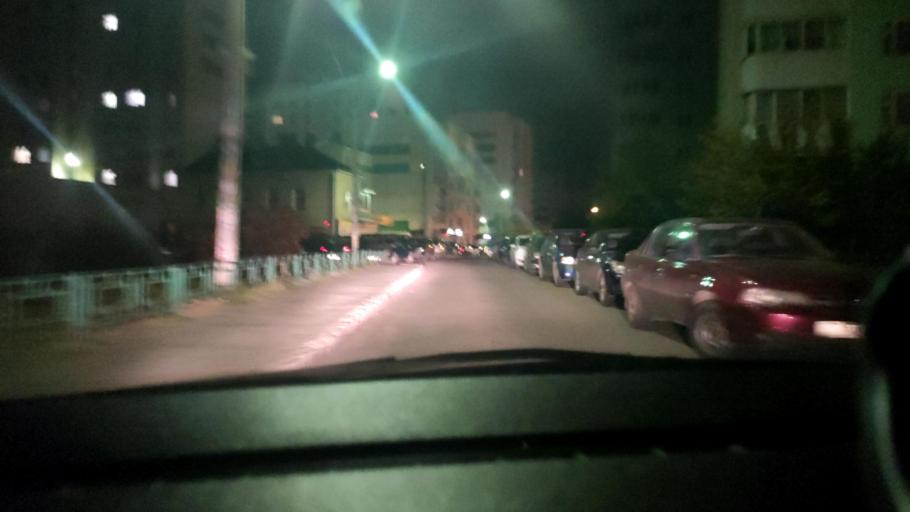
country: RU
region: Voronezj
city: Podgornoye
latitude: 51.7301
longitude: 39.2041
